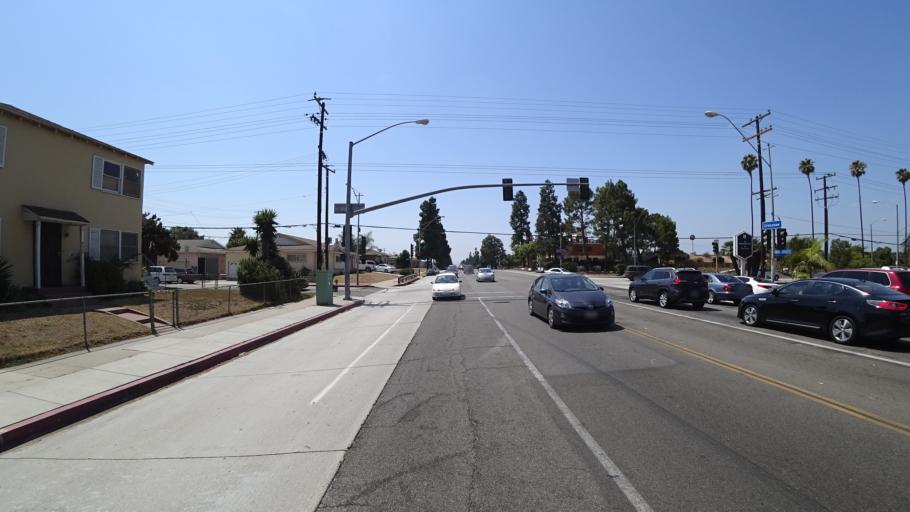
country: US
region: California
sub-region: Los Angeles County
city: Inglewood
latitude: 33.9565
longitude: -118.3264
